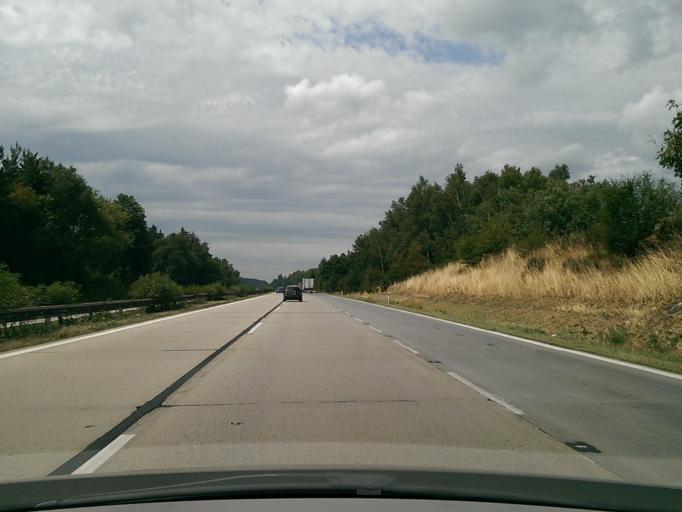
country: CZ
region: Vysocina
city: Merin
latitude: 49.4042
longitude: 15.8397
